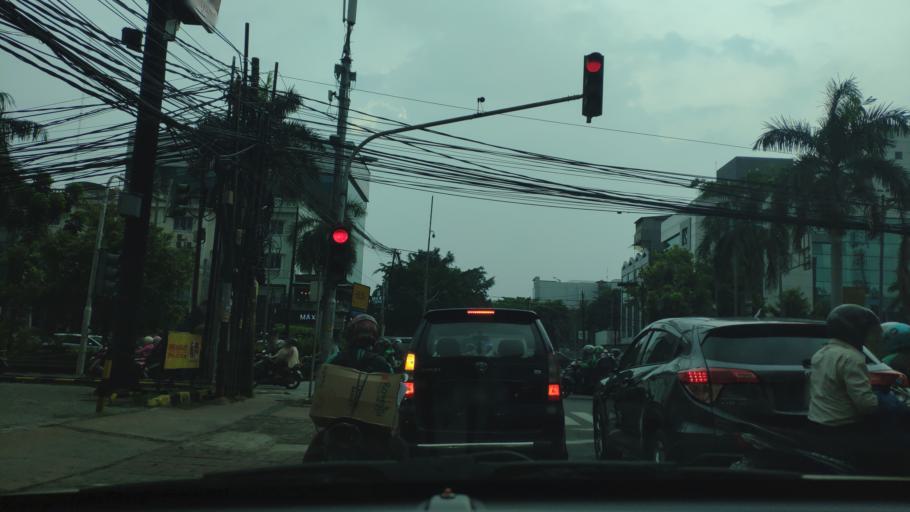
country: ID
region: Jakarta Raya
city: Jakarta
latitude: -6.1756
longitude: 106.8123
